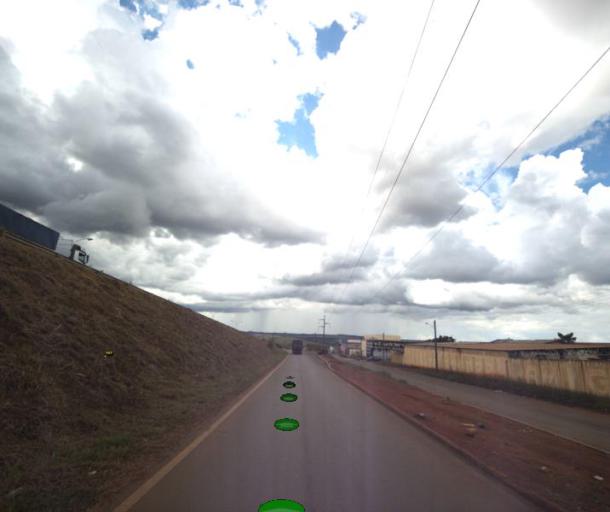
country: BR
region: Goias
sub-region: Anapolis
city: Anapolis
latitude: -16.3235
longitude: -48.9218
